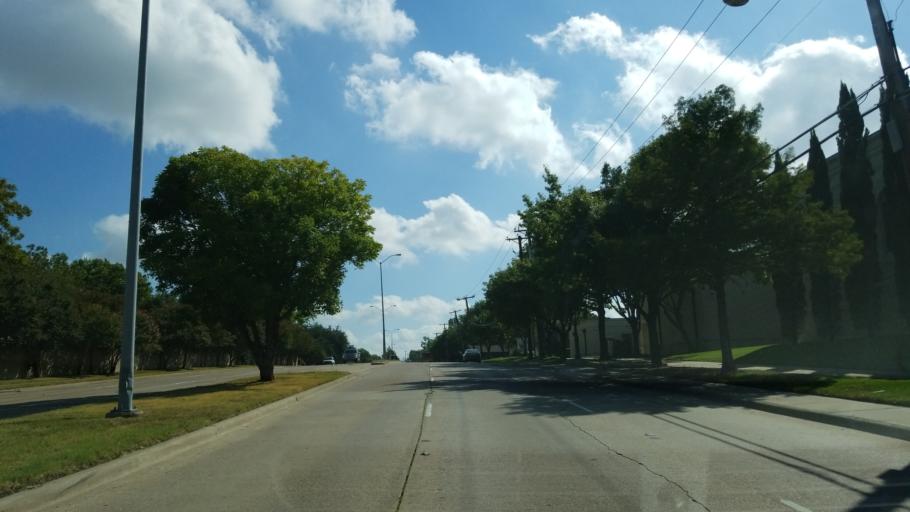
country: US
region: Texas
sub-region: Dallas County
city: Addison
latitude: 32.9498
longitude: -96.7975
